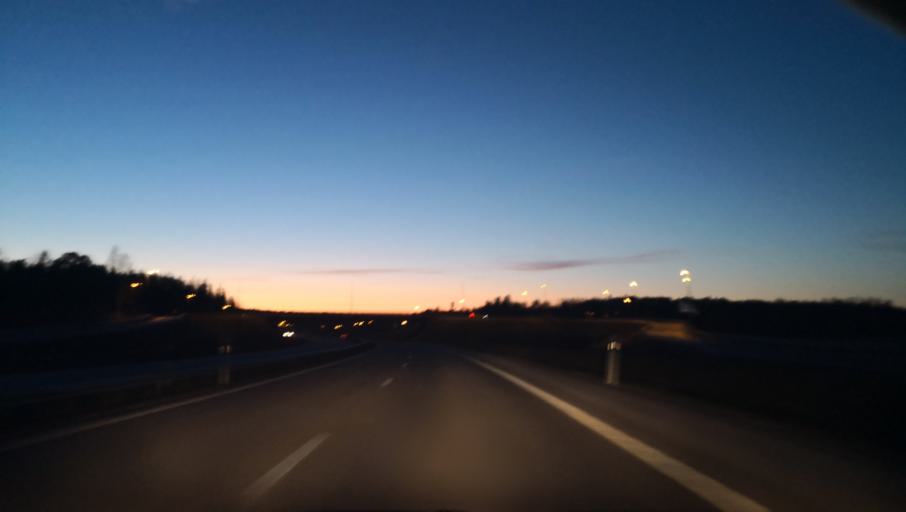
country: SE
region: Stockholm
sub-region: Nynashamns Kommun
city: Osmo
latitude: 58.9420
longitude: 17.9162
